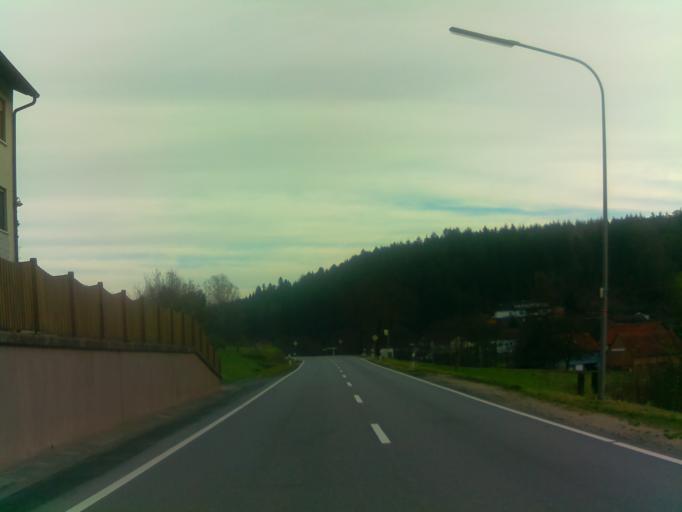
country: DE
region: Hesse
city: Reichelsheim
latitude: 49.6412
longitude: 8.8973
